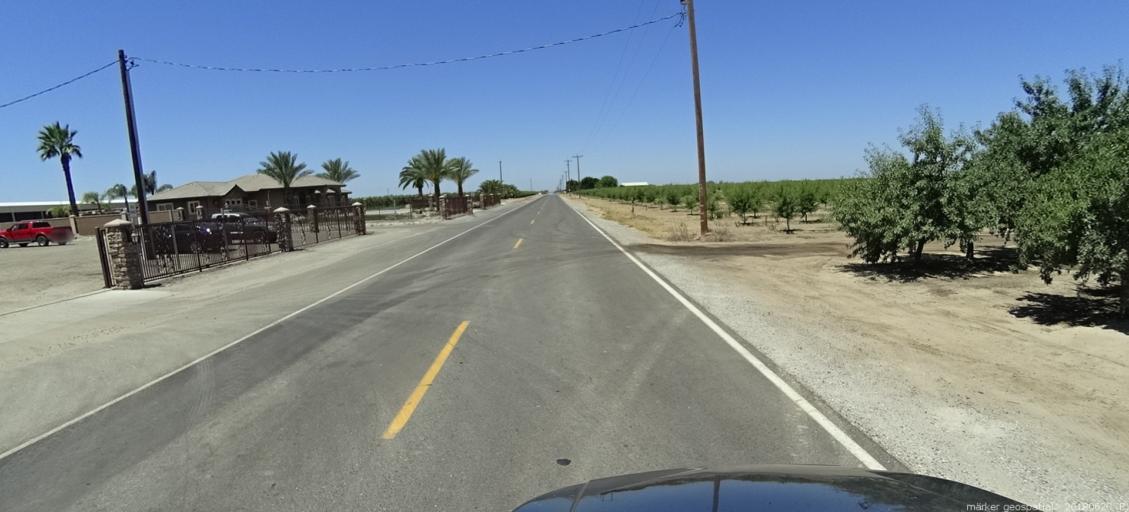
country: US
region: California
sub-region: Madera County
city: Parkwood
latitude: 36.8803
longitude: -119.9876
